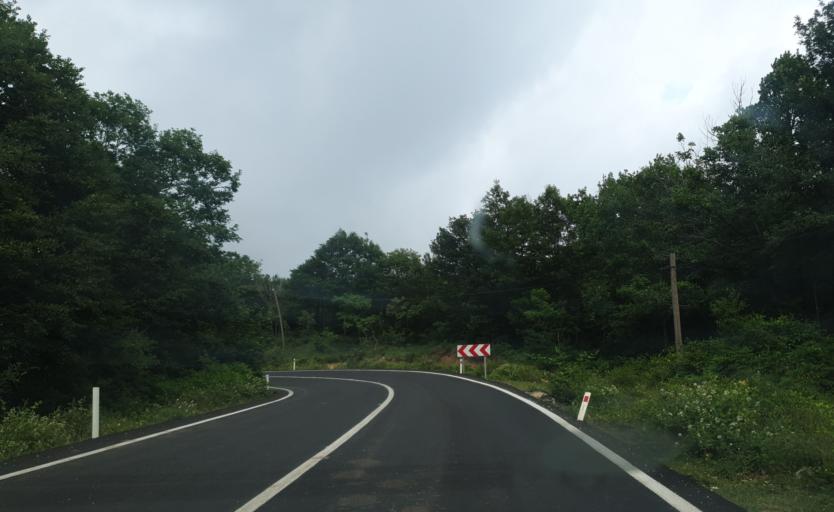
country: TR
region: Kirklareli
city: Salmydessus
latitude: 41.5884
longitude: 28.0713
